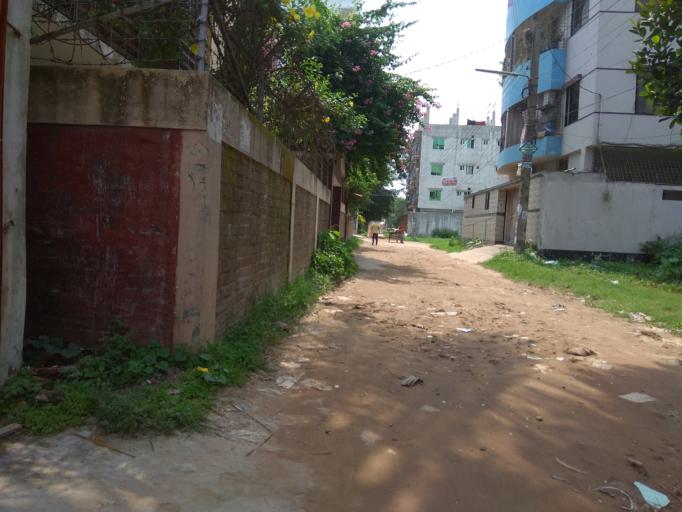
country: BD
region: Dhaka
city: Tungi
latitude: 23.8270
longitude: 90.3515
